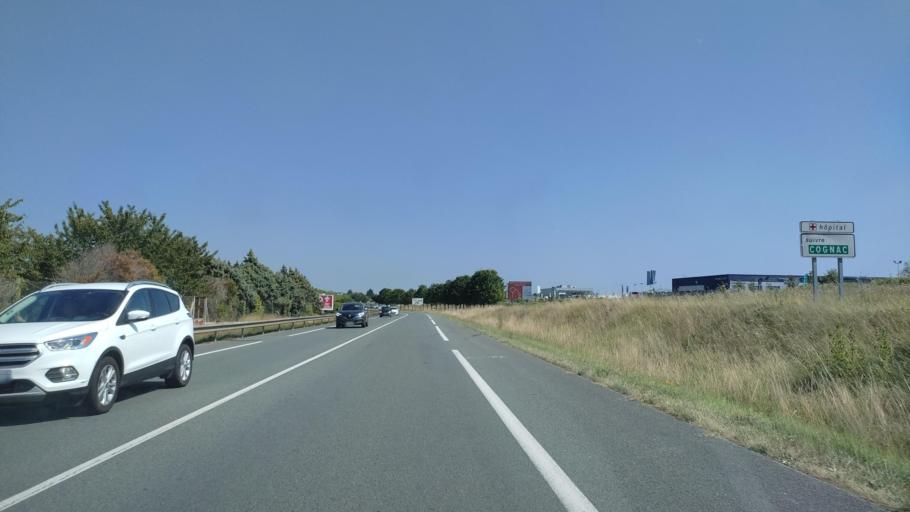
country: FR
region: Poitou-Charentes
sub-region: Departement de la Charente
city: Saint-Brice
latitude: 45.6820
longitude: -0.2990
